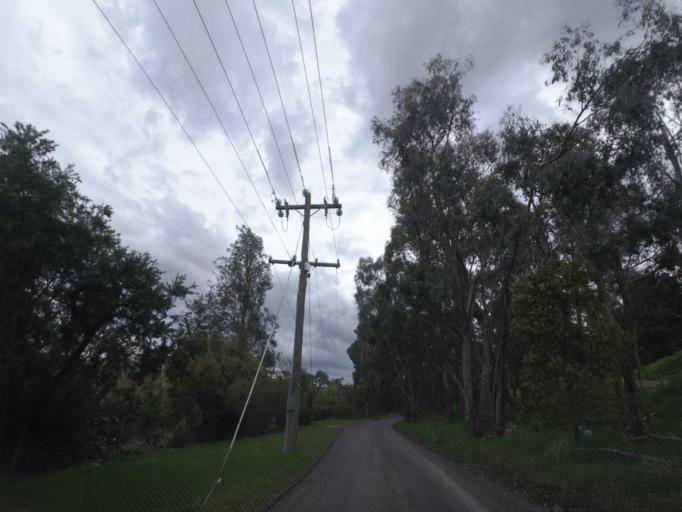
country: AU
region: Victoria
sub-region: Yarra Ranges
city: Mount Evelyn
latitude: -37.7696
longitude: 145.4128
